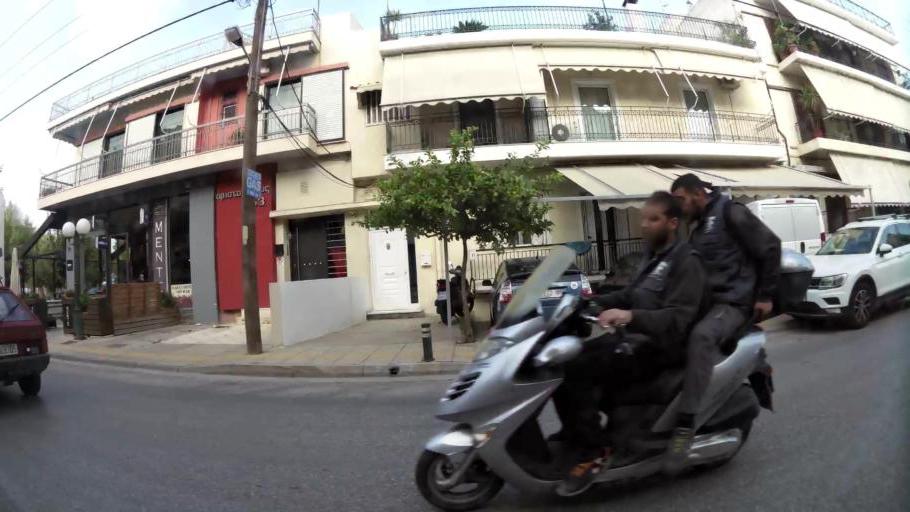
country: GR
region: Attica
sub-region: Nomarchia Anatolikis Attikis
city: Acharnes
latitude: 38.0885
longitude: 23.7436
